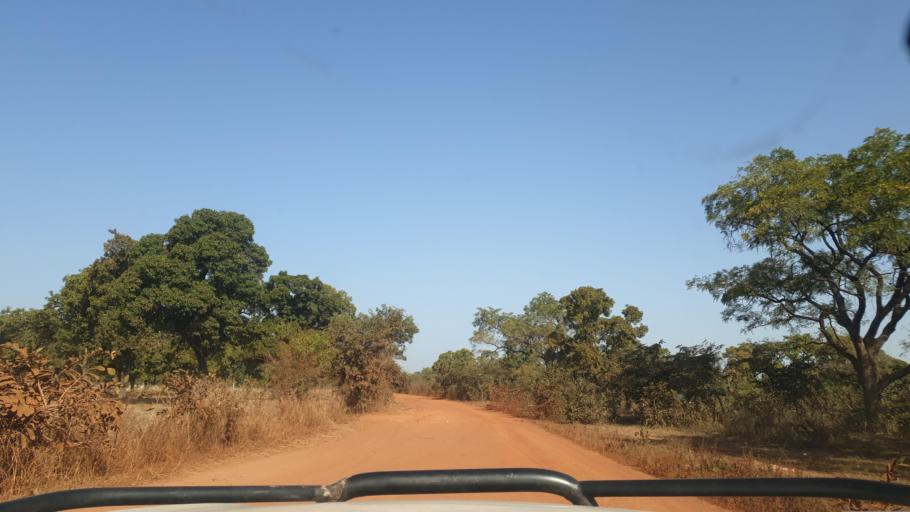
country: ML
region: Sikasso
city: Kolondieba
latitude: 11.7434
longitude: -6.8959
